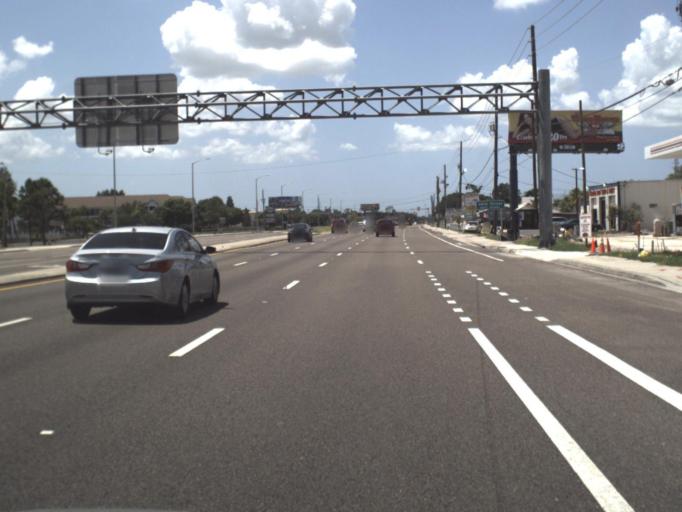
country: US
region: Florida
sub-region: Pinellas County
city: South Highpoint
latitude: 27.8938
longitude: -82.7233
